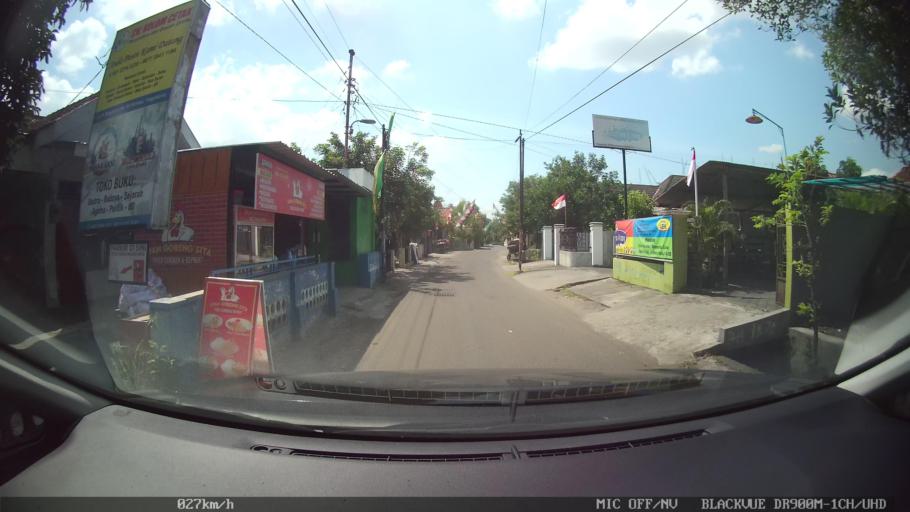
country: ID
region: Daerah Istimewa Yogyakarta
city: Yogyakarta
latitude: -7.8290
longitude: 110.3826
